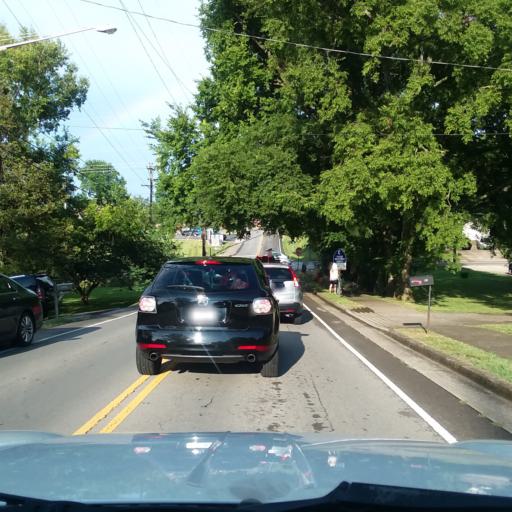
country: US
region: Tennessee
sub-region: Davidson County
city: Oak Hill
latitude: 36.0652
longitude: -86.7601
